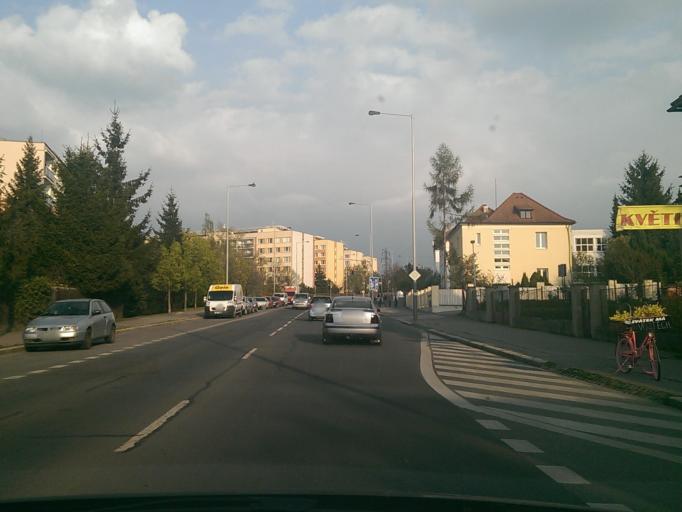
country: CZ
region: Praha
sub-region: Praha 14
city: Hostavice
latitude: 50.0492
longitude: 14.5412
